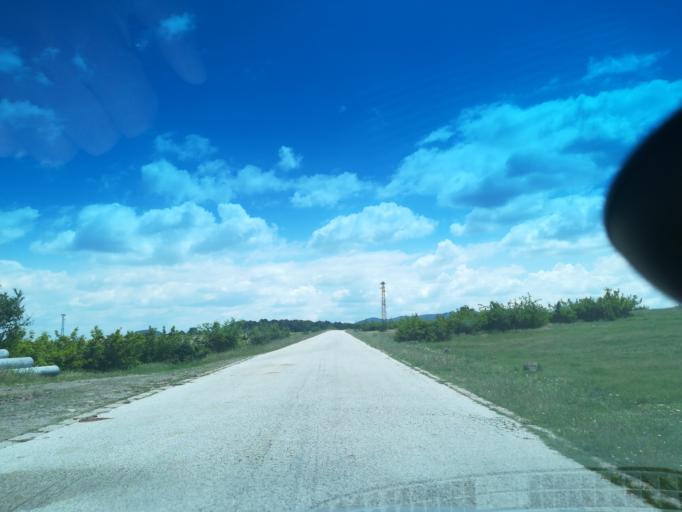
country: BG
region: Khaskovo
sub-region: Obshtina Mineralni Bani
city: Mineralni Bani
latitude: 41.9590
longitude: 25.2607
